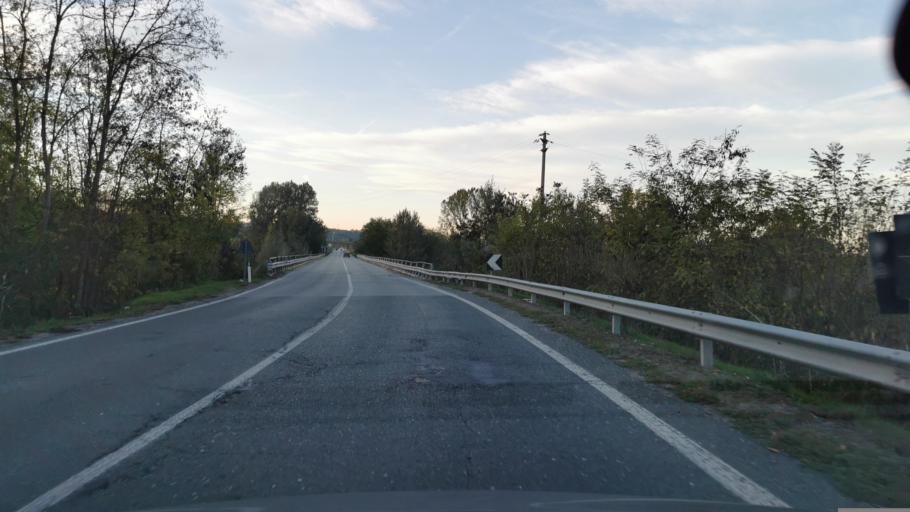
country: IT
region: Piedmont
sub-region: Provincia di Cuneo
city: Cherasco
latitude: 44.6249
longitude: 7.8804
